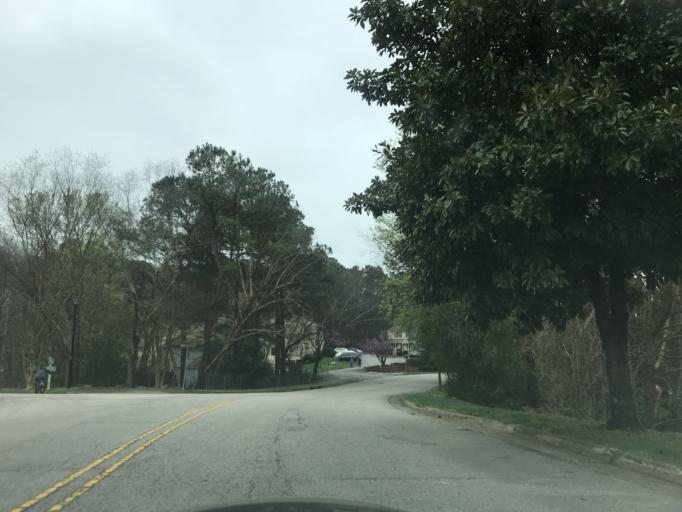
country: US
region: North Carolina
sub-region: Wake County
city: West Raleigh
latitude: 35.8721
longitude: -78.6483
